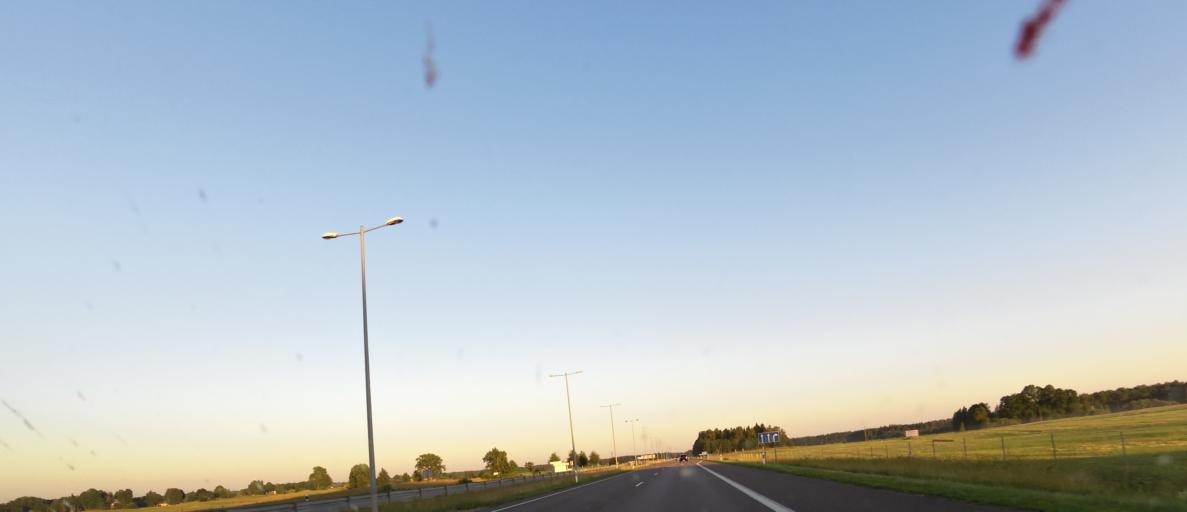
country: LT
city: Sirvintos
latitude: 55.1219
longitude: 24.8420
